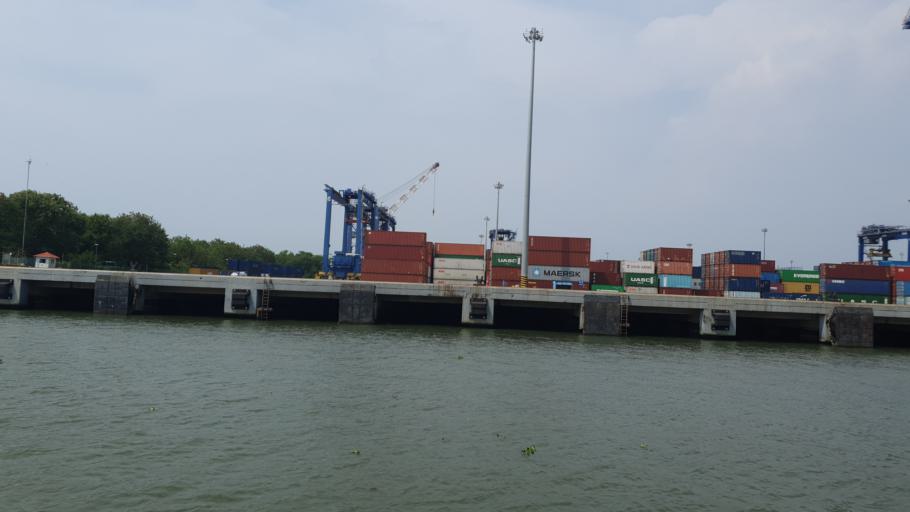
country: IN
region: Kerala
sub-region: Ernakulam
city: Cochin
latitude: 9.9764
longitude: 76.2504
